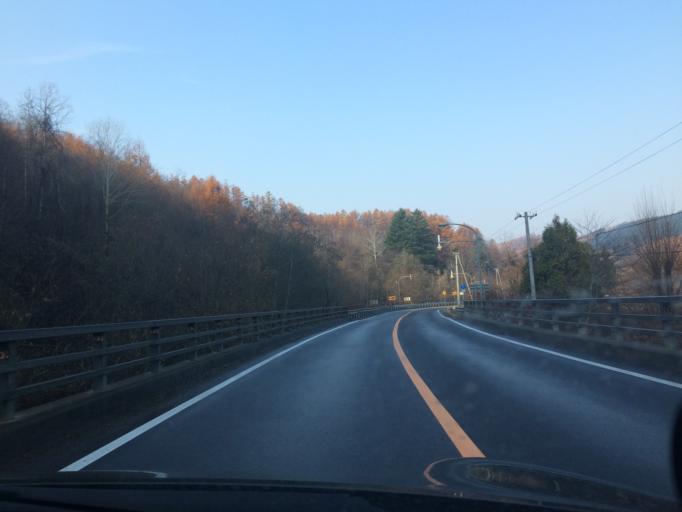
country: JP
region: Hokkaido
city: Iwamizawa
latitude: 42.9291
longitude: 142.0971
